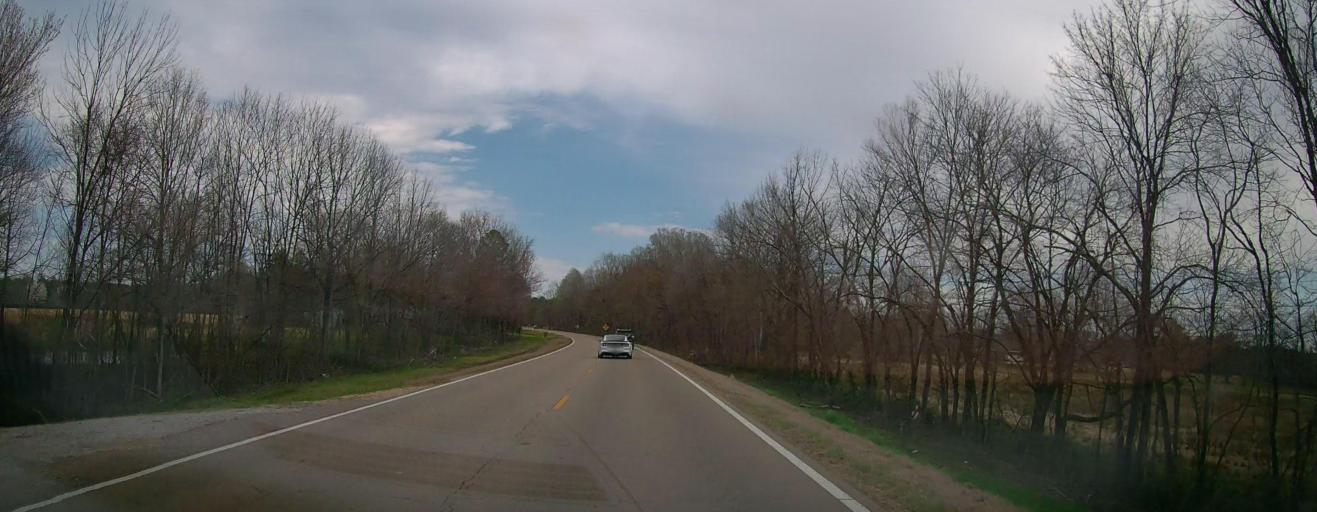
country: US
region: Mississippi
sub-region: Itawamba County
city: Fulton
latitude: 34.2517
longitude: -88.4707
